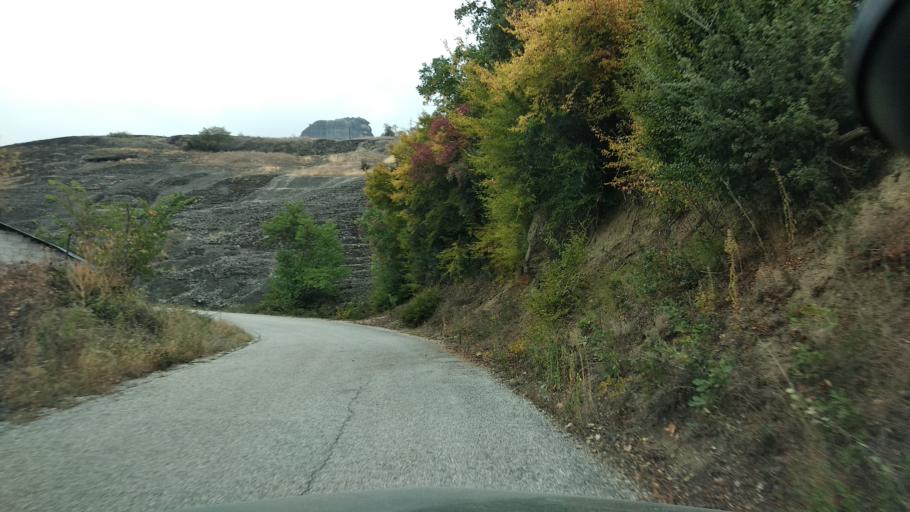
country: GR
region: Thessaly
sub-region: Trikala
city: Kastraki
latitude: 39.7131
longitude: 21.6194
